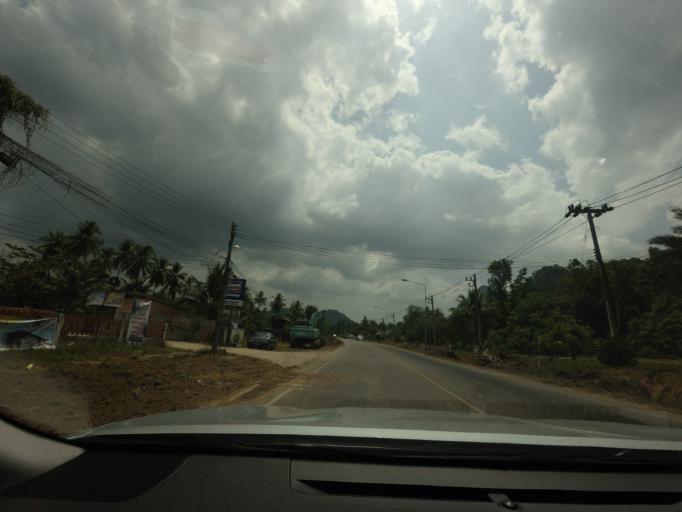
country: TH
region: Phangnga
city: Ban Ao Nang
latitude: 8.1008
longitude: 98.8018
